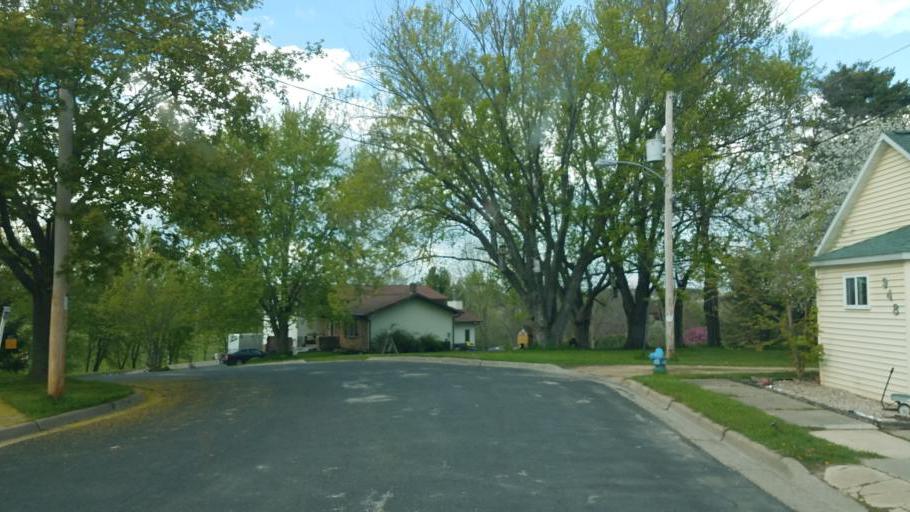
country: US
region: Wisconsin
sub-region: Vernon County
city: Hillsboro
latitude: 43.6548
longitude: -90.3420
